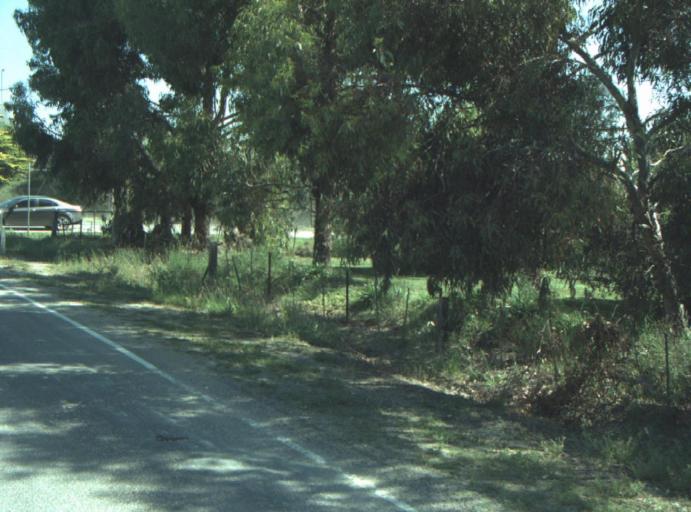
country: AU
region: Victoria
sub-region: Greater Geelong
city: Lara
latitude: -38.0170
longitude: 144.3974
